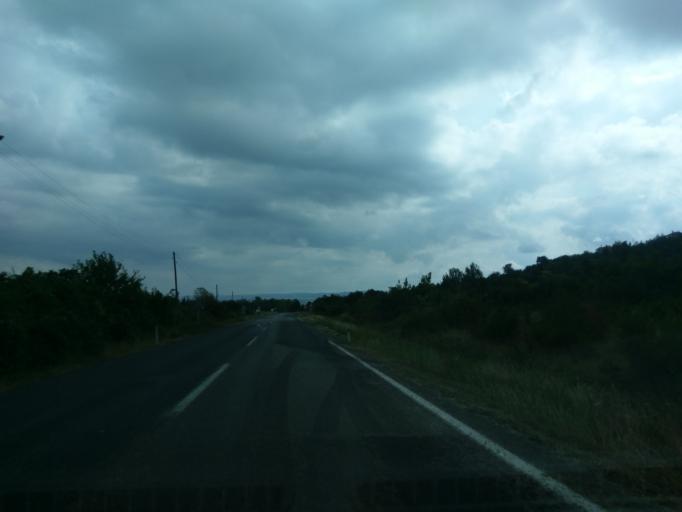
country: TR
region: Sinop
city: Ayancik
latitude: 41.9440
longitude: 34.6867
